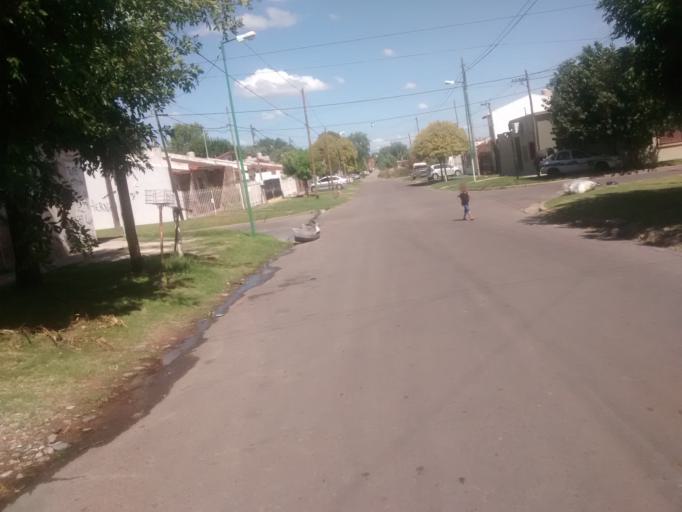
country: AR
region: Buenos Aires
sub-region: Partido de La Plata
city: La Plata
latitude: -34.9433
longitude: -57.9298
